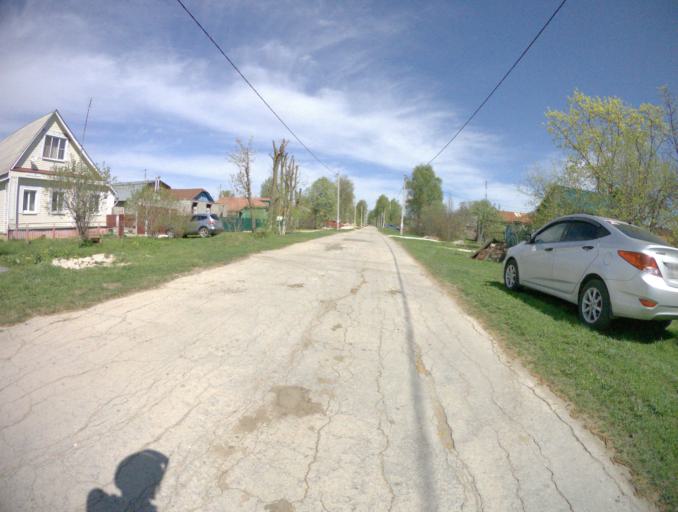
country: RU
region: Vladimir
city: Orgtrud
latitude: 56.2071
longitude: 40.5725
